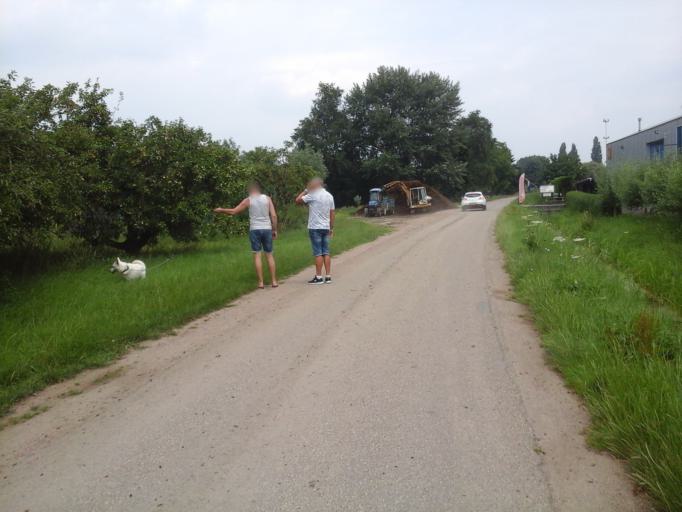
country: NL
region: Gelderland
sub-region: Gemeente Geldermalsen
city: Geldermalsen
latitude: 51.8960
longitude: 5.2742
